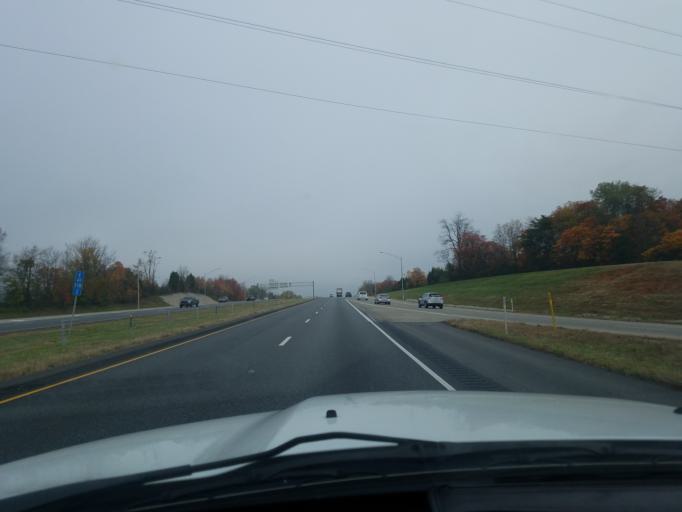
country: US
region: Indiana
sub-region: Floyd County
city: Georgetown
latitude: 38.2895
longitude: -85.9092
